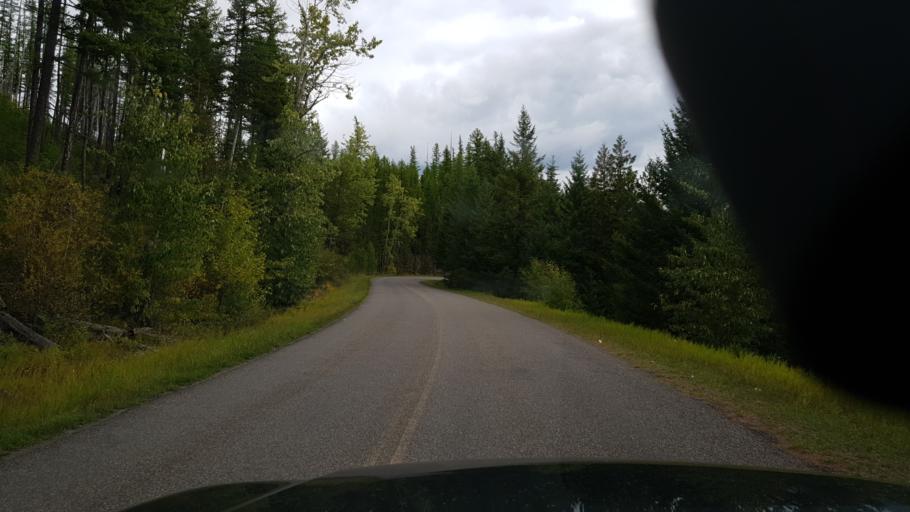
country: US
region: Montana
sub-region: Flathead County
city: Columbia Falls
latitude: 48.5429
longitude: -113.9913
